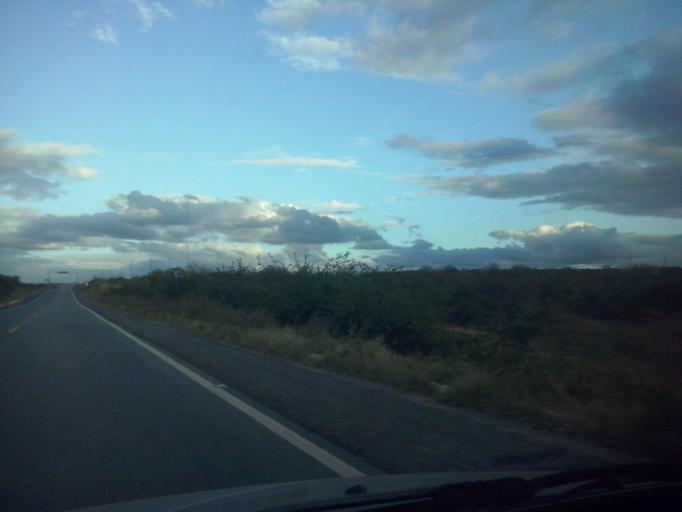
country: BR
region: Paraiba
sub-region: Patos
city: Patos
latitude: -7.0004
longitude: -37.3075
